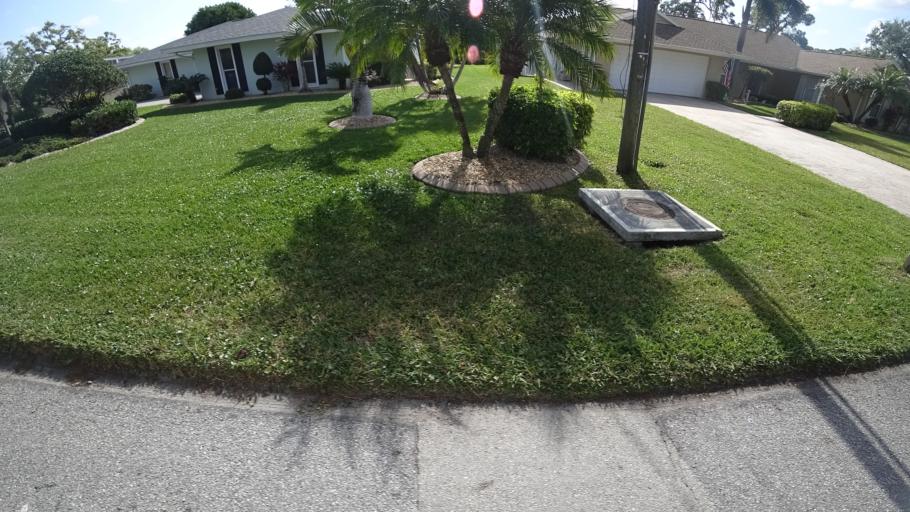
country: US
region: Florida
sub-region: Manatee County
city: Whitfield
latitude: 27.4234
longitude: -82.5622
